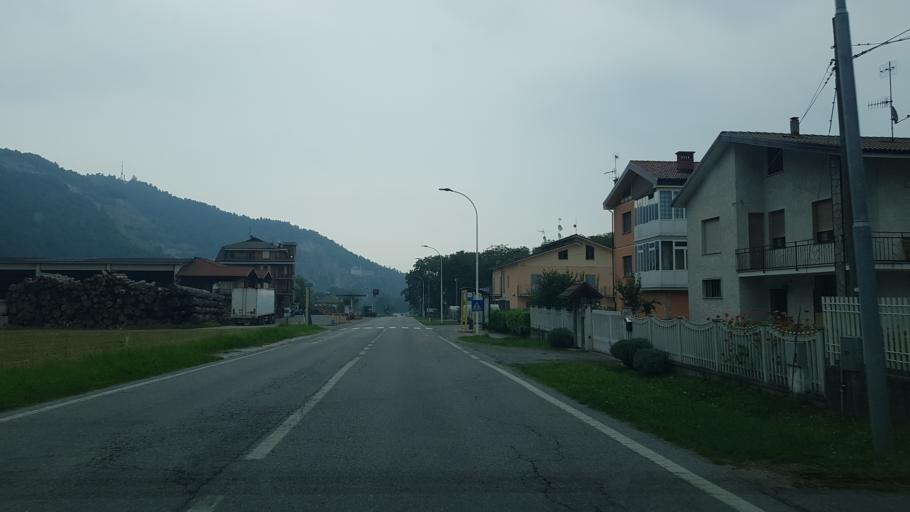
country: IT
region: Piedmont
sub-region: Provincia di Cuneo
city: Roccaforte Mondovi
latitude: 44.3211
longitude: 7.7450
